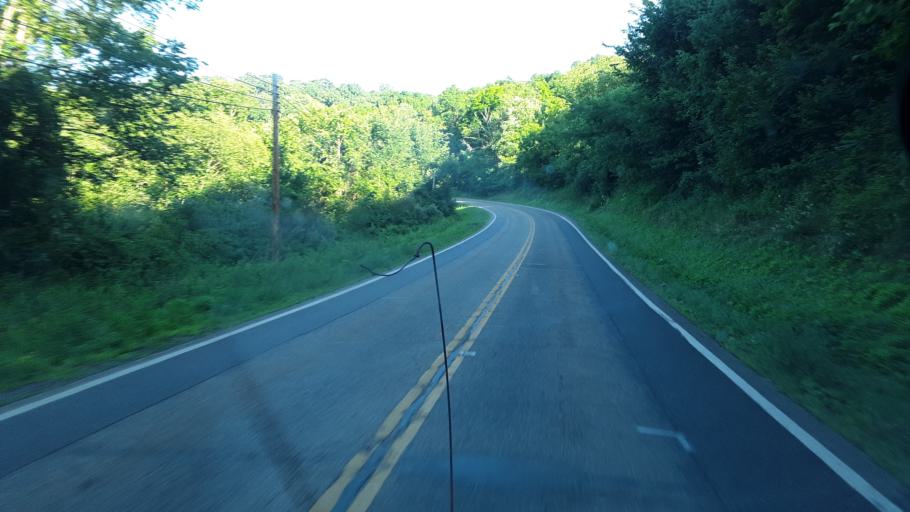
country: US
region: Ohio
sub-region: Carroll County
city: Carrollton
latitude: 40.5503
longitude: -81.1652
